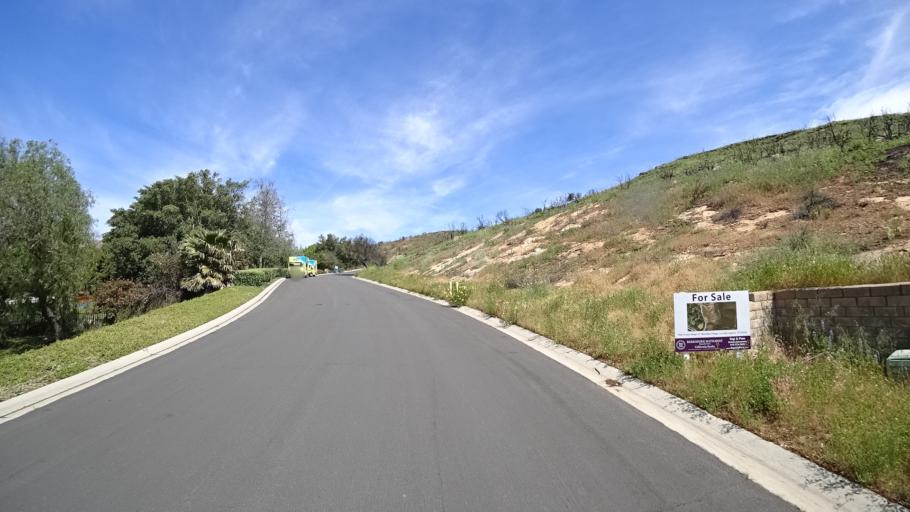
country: US
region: California
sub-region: Ventura County
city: Oak Park
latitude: 34.1932
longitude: -118.7988
